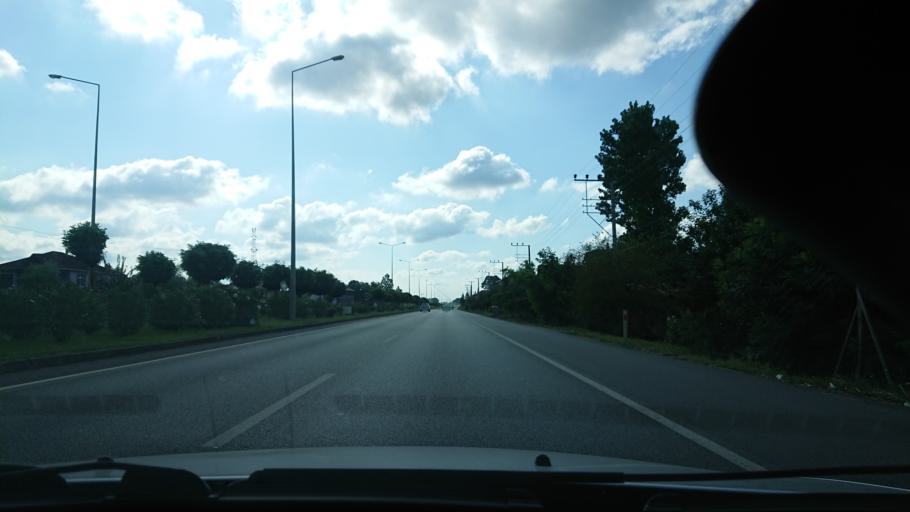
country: TR
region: Samsun
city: Terme
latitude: 41.2165
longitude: 36.9224
